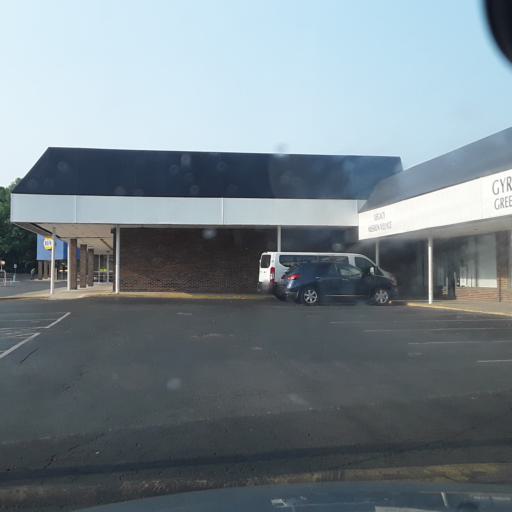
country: US
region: Tennessee
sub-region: Williamson County
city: Brentwood
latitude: 36.0584
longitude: -86.7172
